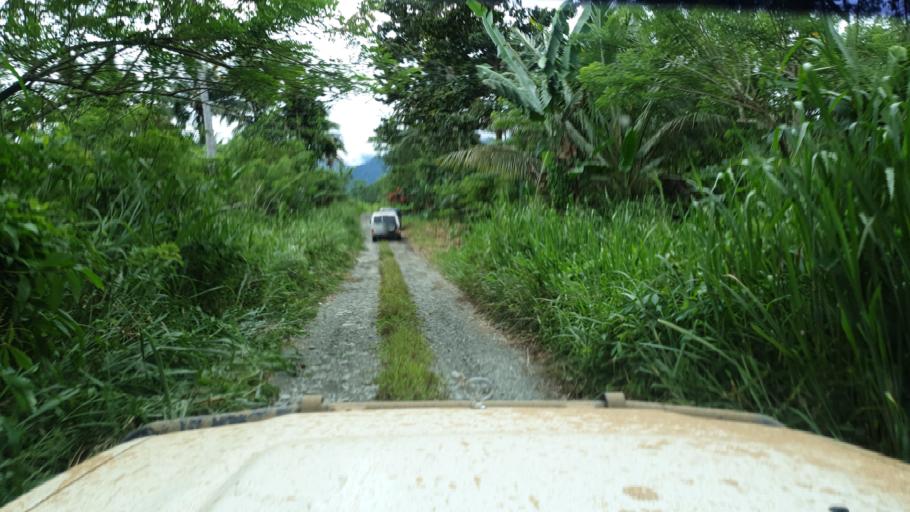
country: PG
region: Northern Province
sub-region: Sohe
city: Kokoda
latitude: -8.9322
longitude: 147.8680
